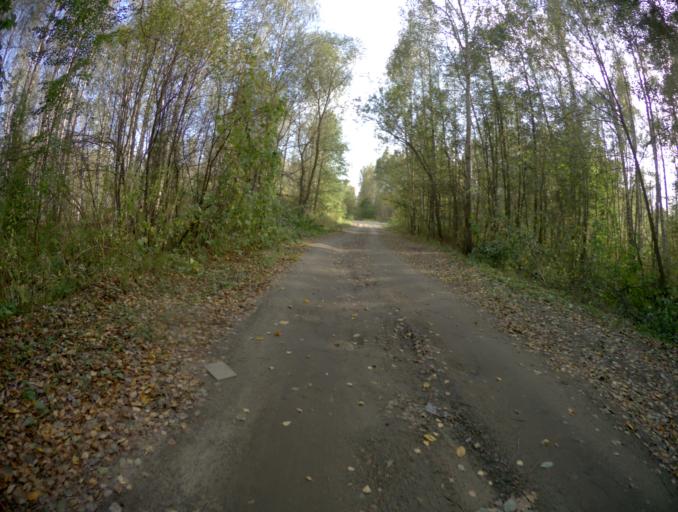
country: RU
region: Vladimir
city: Raduzhnyy
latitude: 56.0021
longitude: 40.2676
